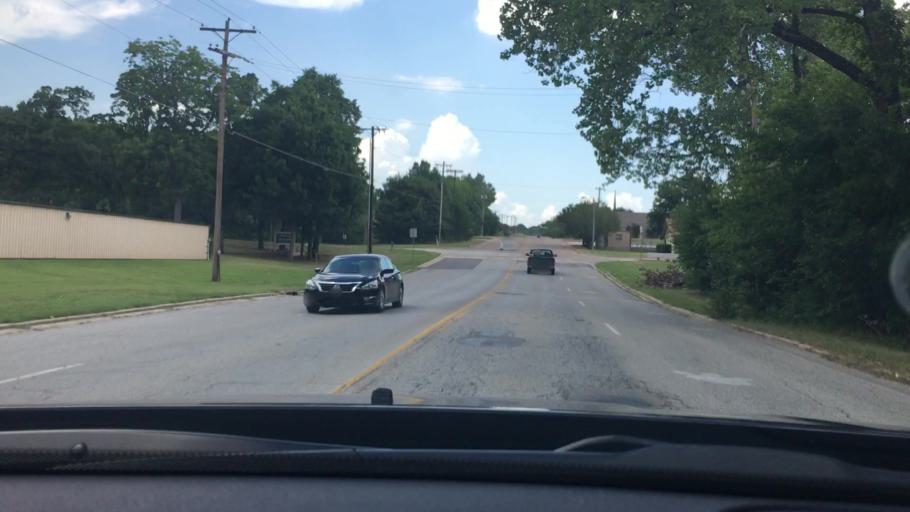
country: US
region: Oklahoma
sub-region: Pontotoc County
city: Ada
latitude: 34.7625
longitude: -96.6612
